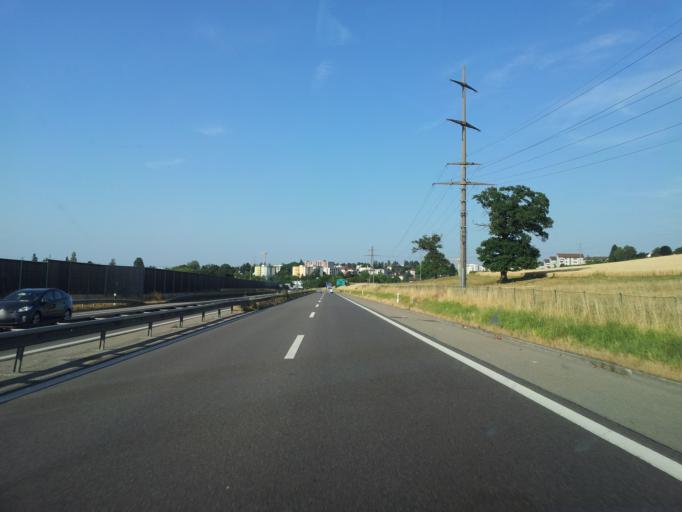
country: CH
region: Fribourg
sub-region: Sarine District
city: Givisiez
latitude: 46.8058
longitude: 7.1323
